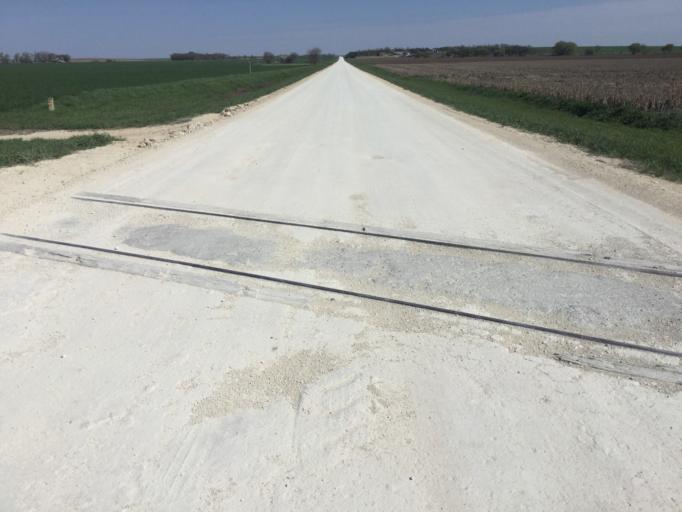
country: US
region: Kansas
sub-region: Osborne County
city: Osborne
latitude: 39.5138
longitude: -98.5816
